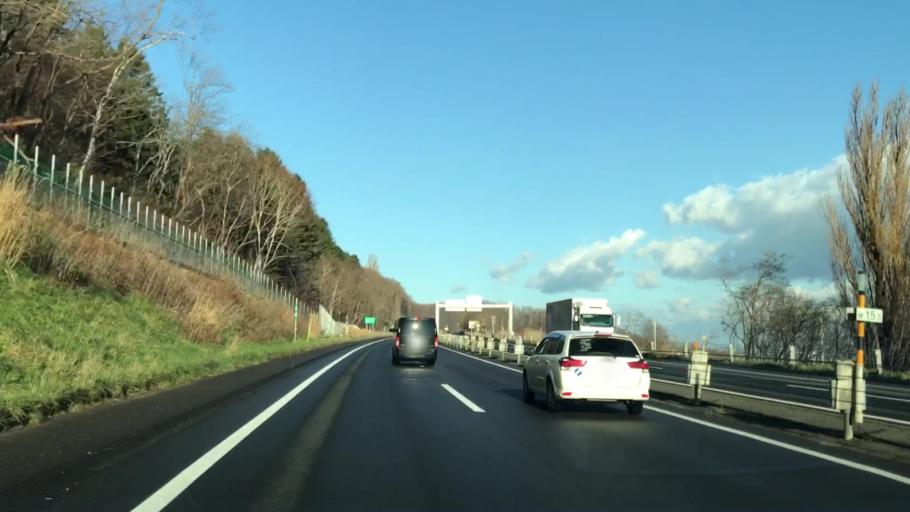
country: JP
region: Hokkaido
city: Sapporo
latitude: 43.0954
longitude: 141.2532
